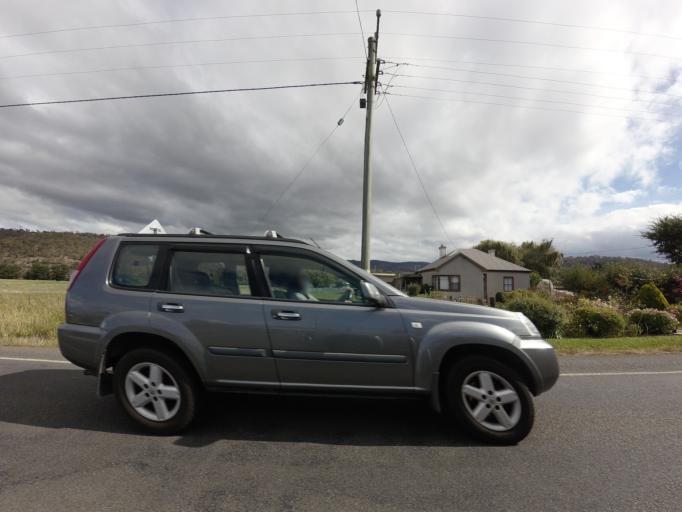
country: AU
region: Tasmania
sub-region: Derwent Valley
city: New Norfolk
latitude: -42.7734
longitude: 147.0346
